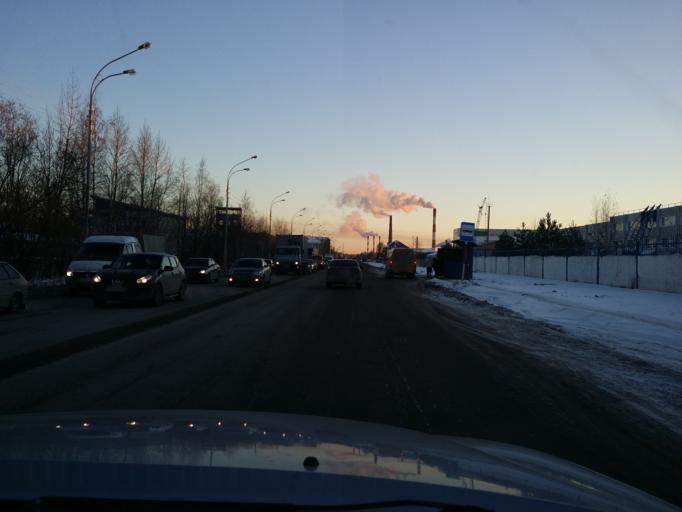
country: RU
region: Khanty-Mansiyskiy Avtonomnyy Okrug
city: Nizhnevartovsk
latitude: 60.9448
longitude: 76.5481
